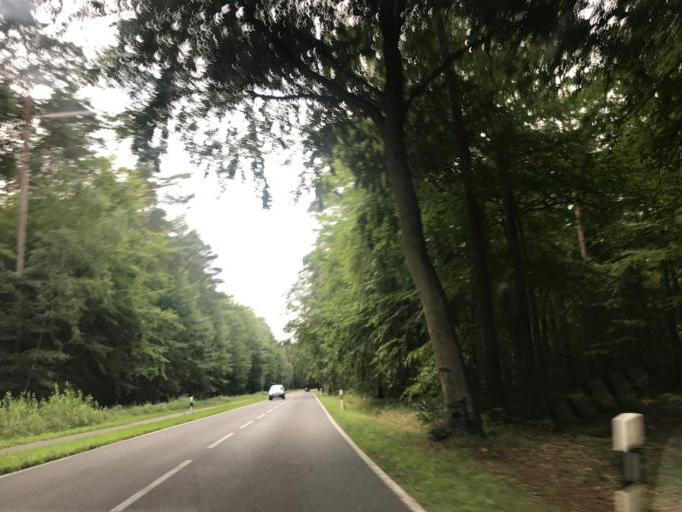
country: DE
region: Brandenburg
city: Rheinsberg
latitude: 53.1135
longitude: 12.9866
